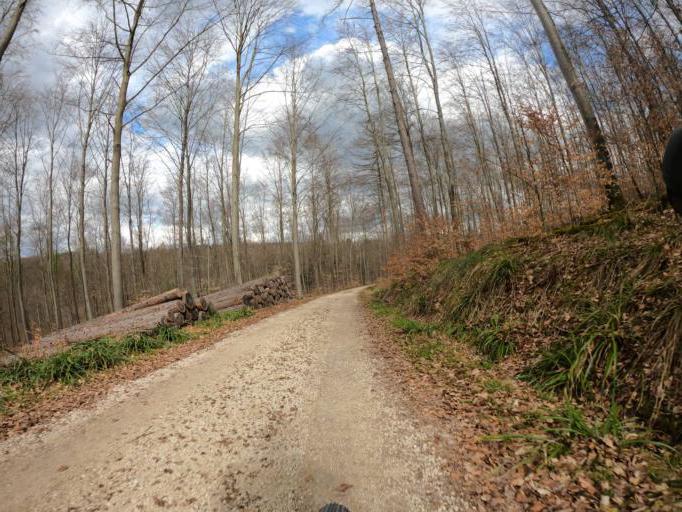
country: DE
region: Baden-Wuerttemberg
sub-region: Tuebingen Region
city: Gomaringen
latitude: 48.4315
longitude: 9.1180
